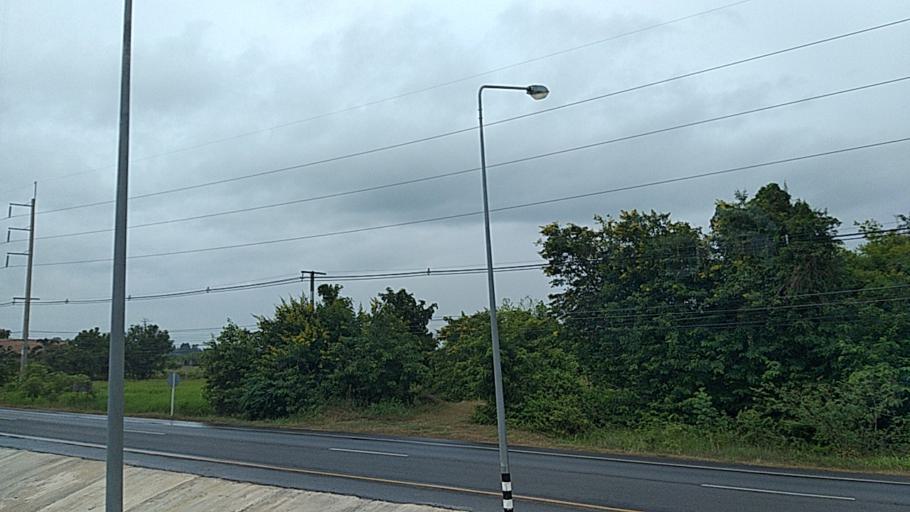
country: TH
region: Maha Sarakham
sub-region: Amphoe Borabue
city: Borabue
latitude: 16.0638
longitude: 103.1418
